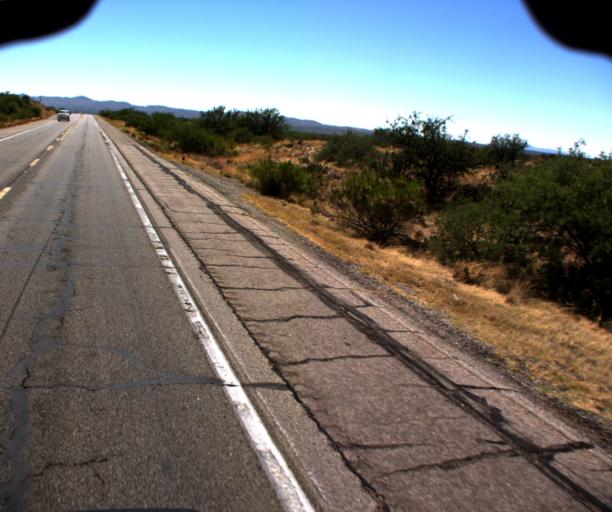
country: US
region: Arizona
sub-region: Pinal County
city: Oracle
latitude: 32.6071
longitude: -110.8556
